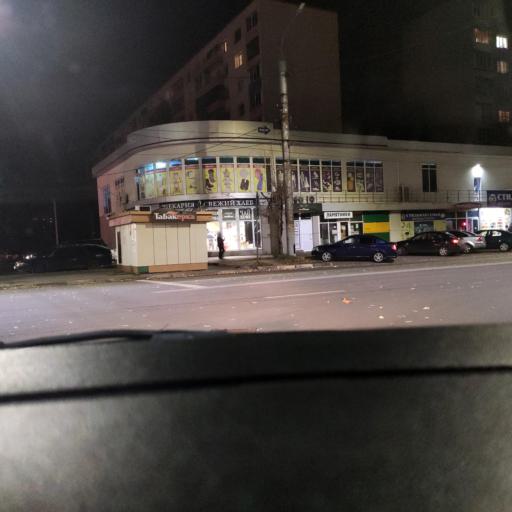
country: RU
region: Voronezj
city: Pridonskoy
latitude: 51.6517
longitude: 39.1212
